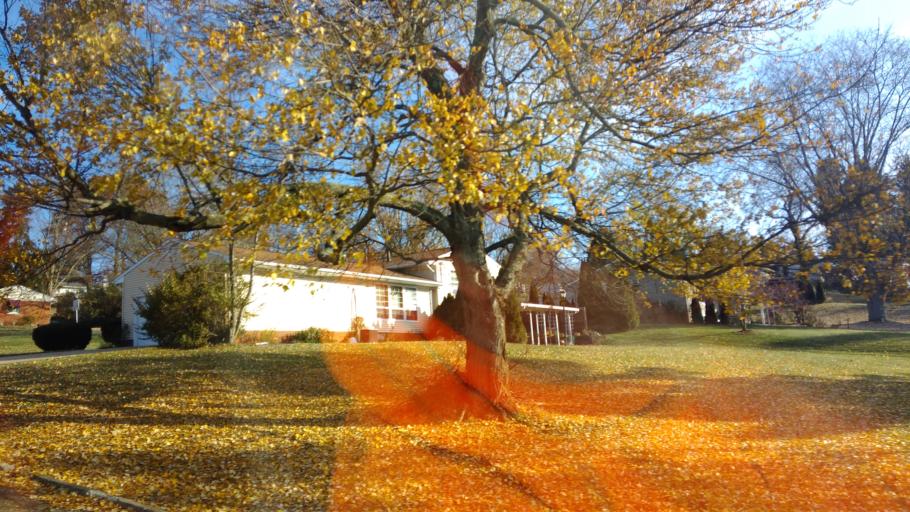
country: US
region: Ohio
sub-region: Richland County
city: Lexington
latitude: 40.6929
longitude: -82.5392
